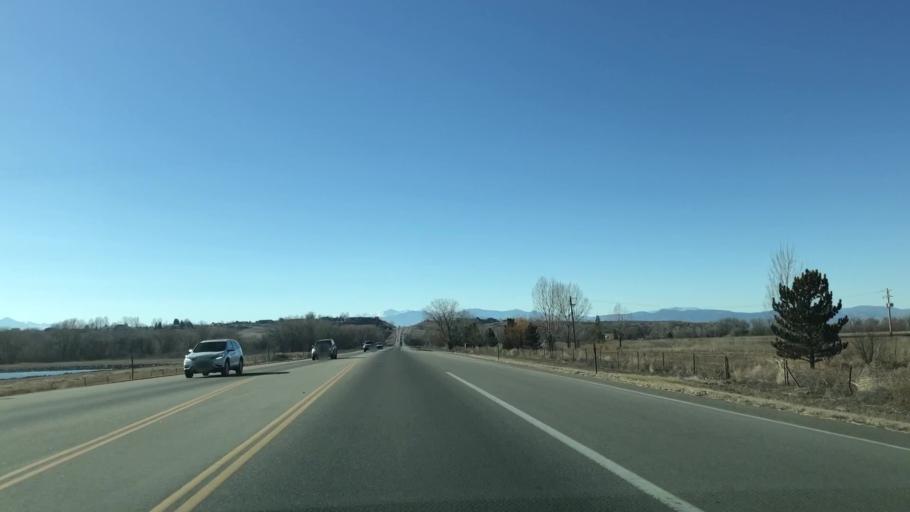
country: US
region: Colorado
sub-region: Weld County
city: Windsor
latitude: 40.4793
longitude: -104.9464
